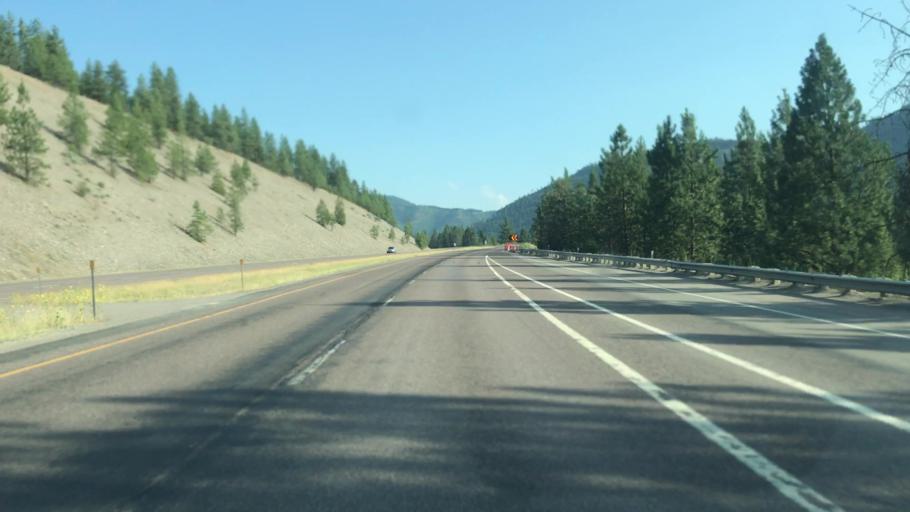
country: US
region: Montana
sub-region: Mineral County
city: Superior
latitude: 47.0222
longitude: -114.7373
